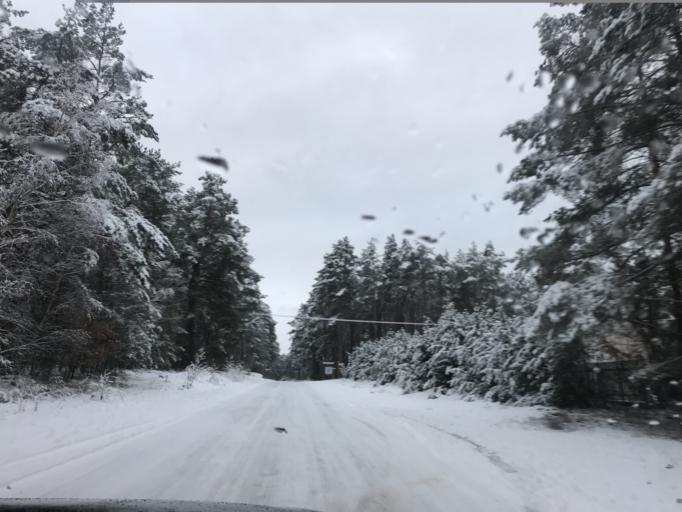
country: PL
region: Pomeranian Voivodeship
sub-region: Powiat bytowski
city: Czarna Dabrowka
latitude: 54.2754
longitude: 17.5881
